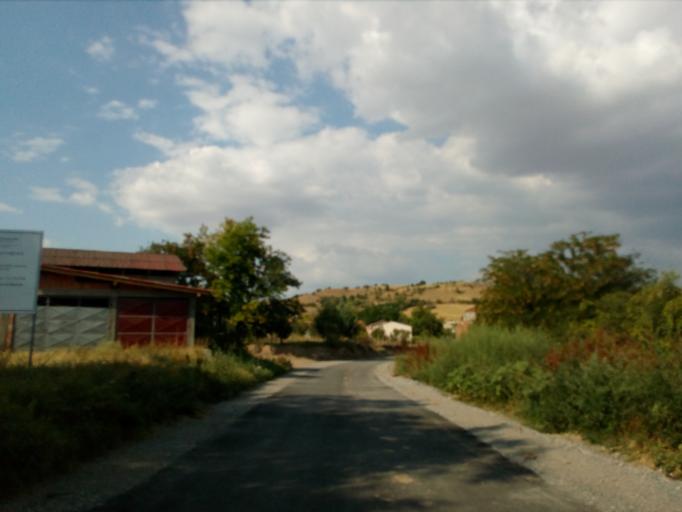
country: MK
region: Veles
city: Veles
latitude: 41.7533
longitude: 21.7948
